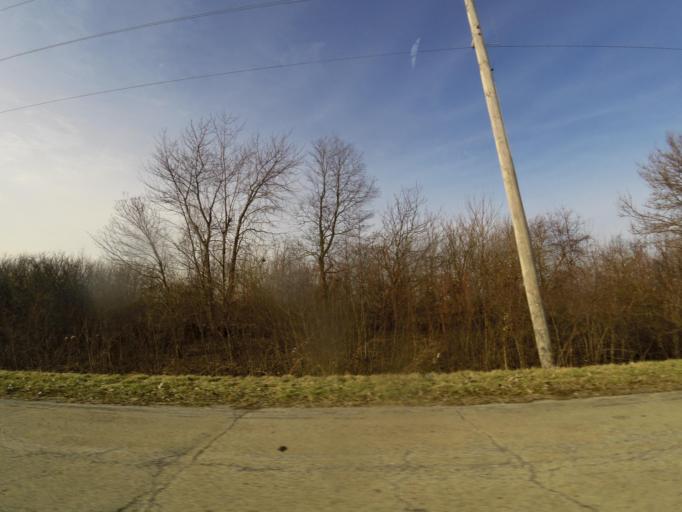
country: US
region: Illinois
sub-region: Macon County
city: Macon
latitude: 39.7692
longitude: -88.9825
